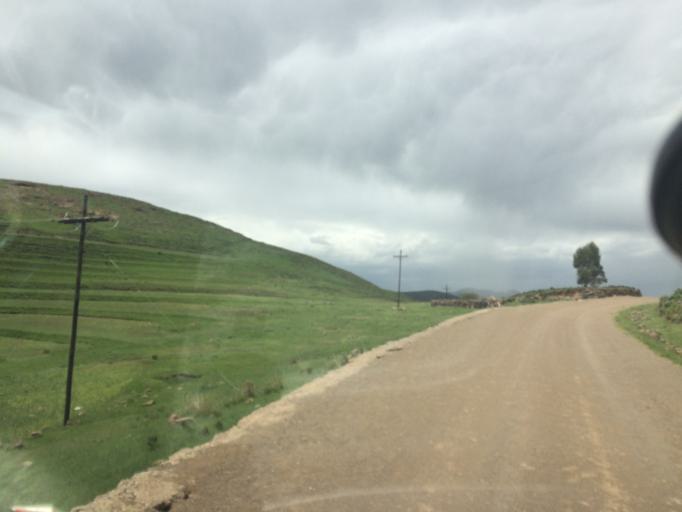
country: LS
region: Maseru
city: Nako
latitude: -29.8466
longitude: 28.0270
